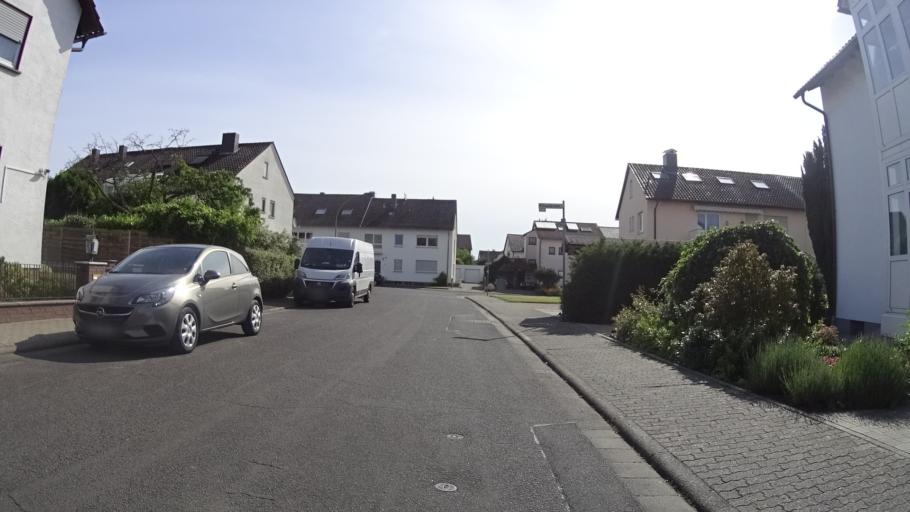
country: DE
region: Bavaria
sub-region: Regierungsbezirk Unterfranken
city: Mainaschaff
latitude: 49.9770
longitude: 9.0937
